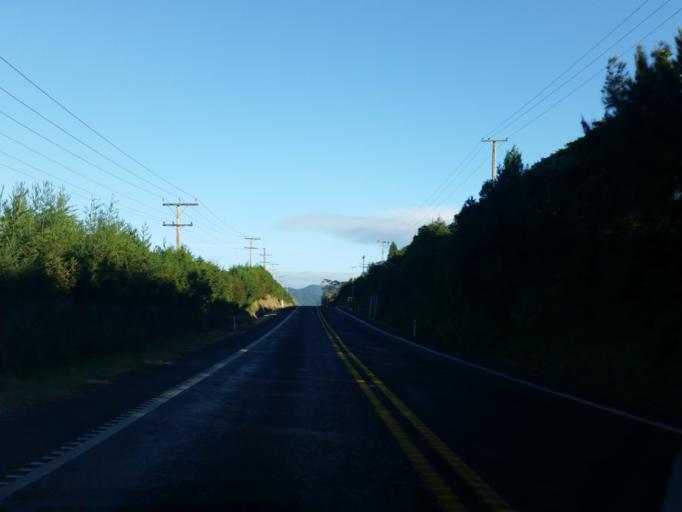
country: NZ
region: Bay of Plenty
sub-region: Western Bay of Plenty District
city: Katikati
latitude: -37.6037
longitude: 175.9340
